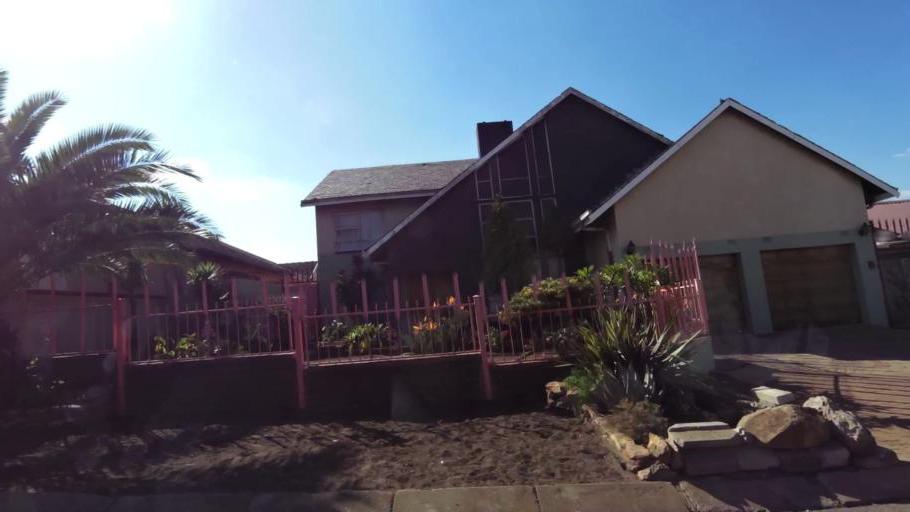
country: ZA
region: Gauteng
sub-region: City of Johannesburg Metropolitan Municipality
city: Soweto
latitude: -26.2394
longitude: 27.9038
